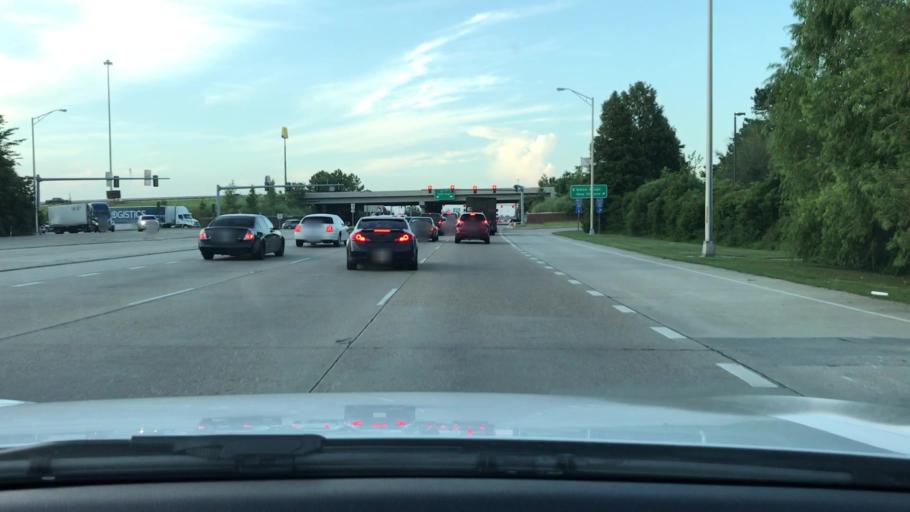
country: US
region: Louisiana
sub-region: East Baton Rouge Parish
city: Village Saint George
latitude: 30.3805
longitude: -91.0668
